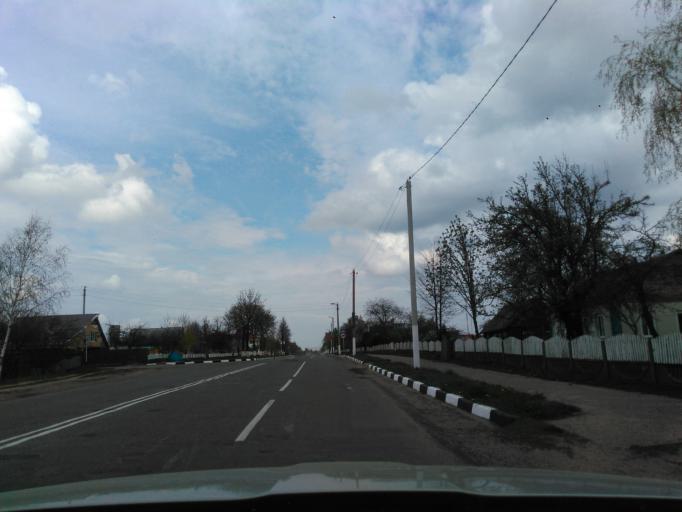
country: BY
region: Vitebsk
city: Chashniki
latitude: 54.8427
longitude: 29.1769
